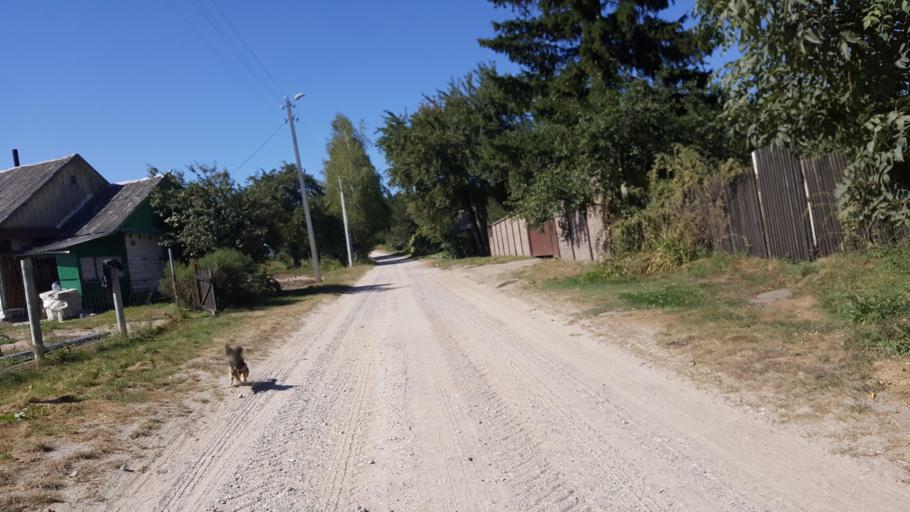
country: PL
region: Lublin Voivodeship
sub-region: Powiat bialski
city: Rokitno
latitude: 52.2246
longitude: 23.3399
